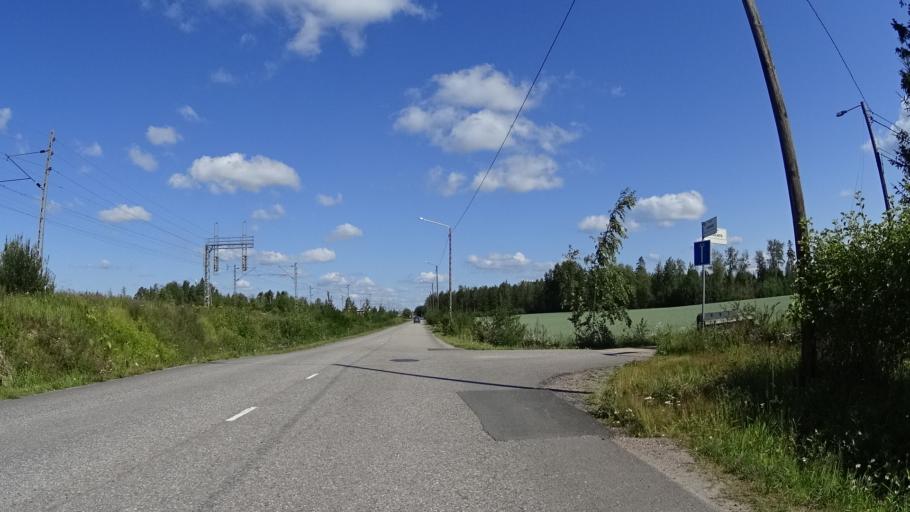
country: FI
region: Uusimaa
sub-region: Helsinki
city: Jaervenpaeae
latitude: 60.4526
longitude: 25.1033
